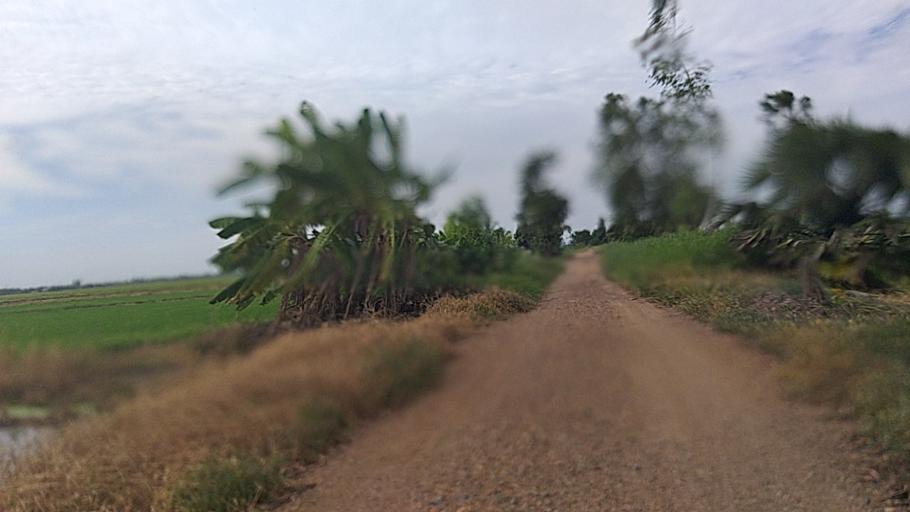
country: TH
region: Pathum Thani
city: Ban Lam Luk Ka
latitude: 14.0323
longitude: 100.8567
